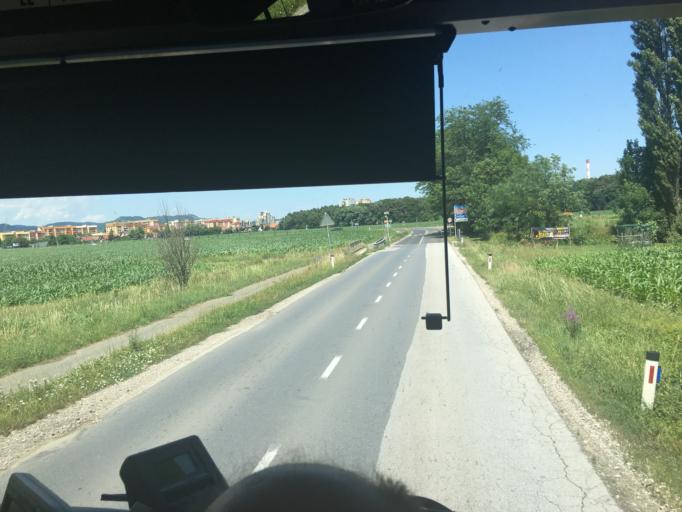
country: SI
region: Maribor
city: Razvanje
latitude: 46.5281
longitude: 15.6374
